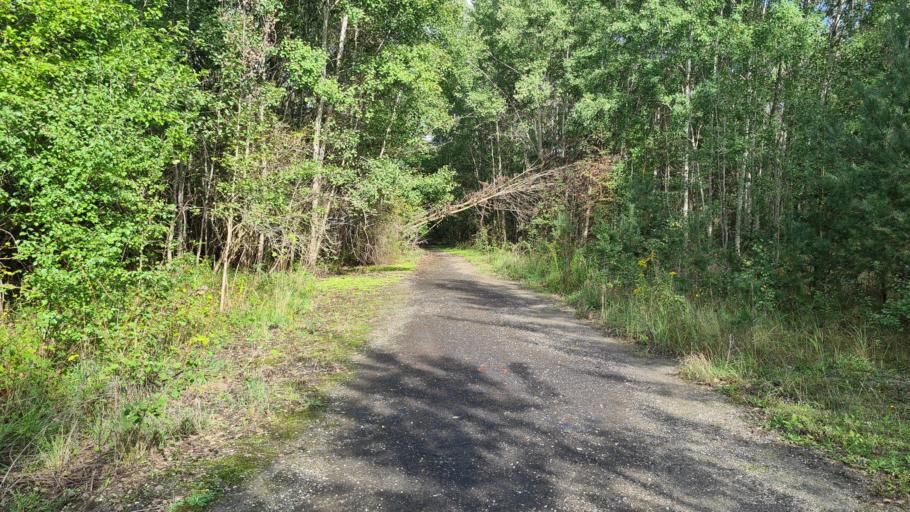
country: DE
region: Brandenburg
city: Sallgast
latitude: 51.5619
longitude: 13.8582
